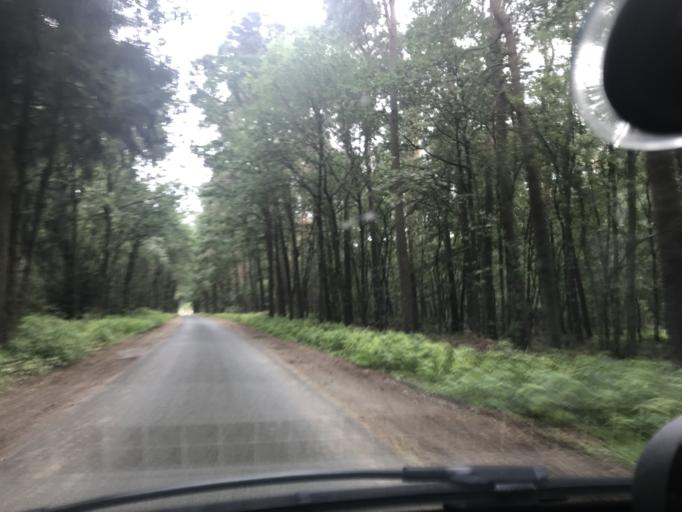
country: DE
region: Lower Saxony
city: Moisburg
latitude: 53.3938
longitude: 9.7246
